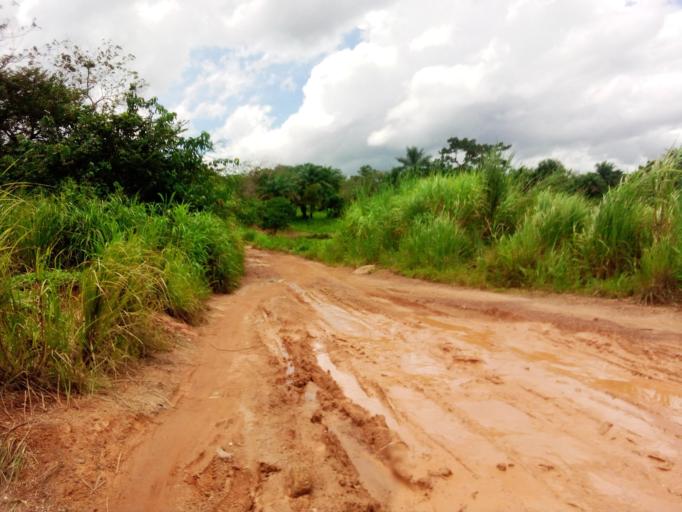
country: SL
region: Eastern Province
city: Simbakoro
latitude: 8.6097
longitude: -10.9849
